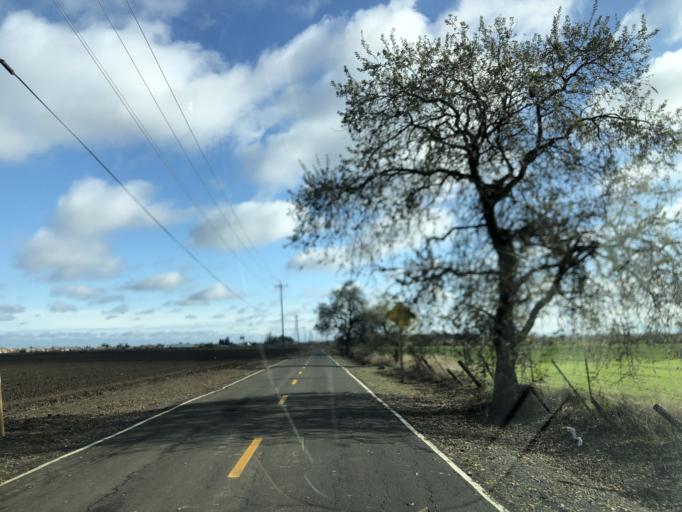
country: US
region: California
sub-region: Contra Costa County
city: Brentwood
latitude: 37.9471
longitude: -121.7497
